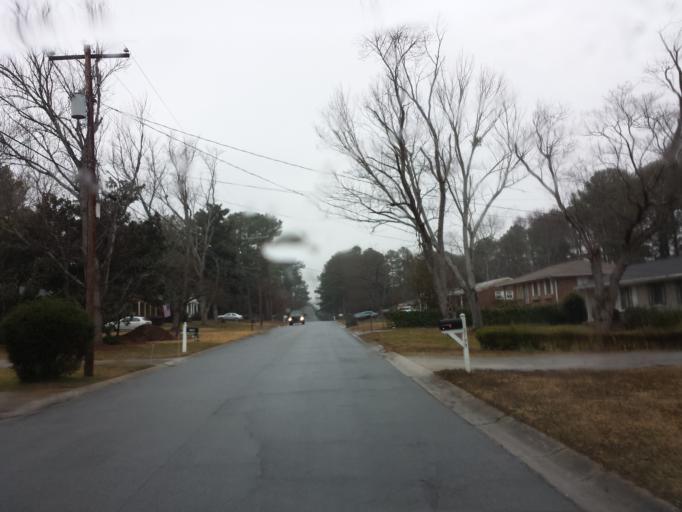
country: US
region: Georgia
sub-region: Cobb County
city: Smyrna
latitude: 33.8845
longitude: -84.4863
